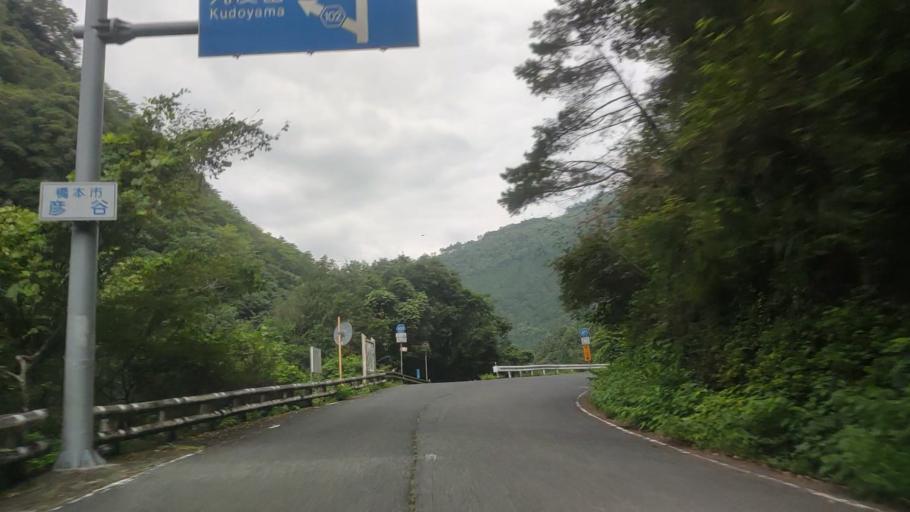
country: JP
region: Wakayama
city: Hashimoto
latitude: 34.2719
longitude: 135.6353
